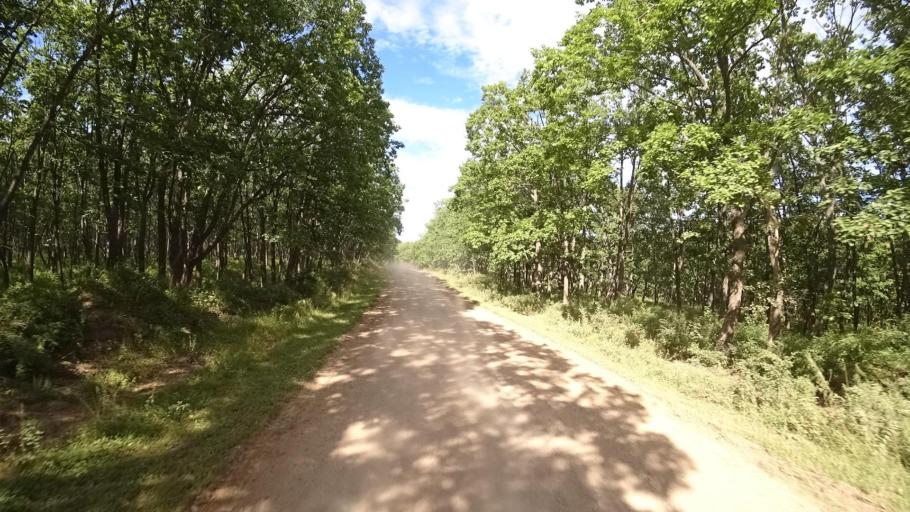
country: RU
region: Primorskiy
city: Yakovlevka
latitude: 44.4078
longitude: 133.5689
